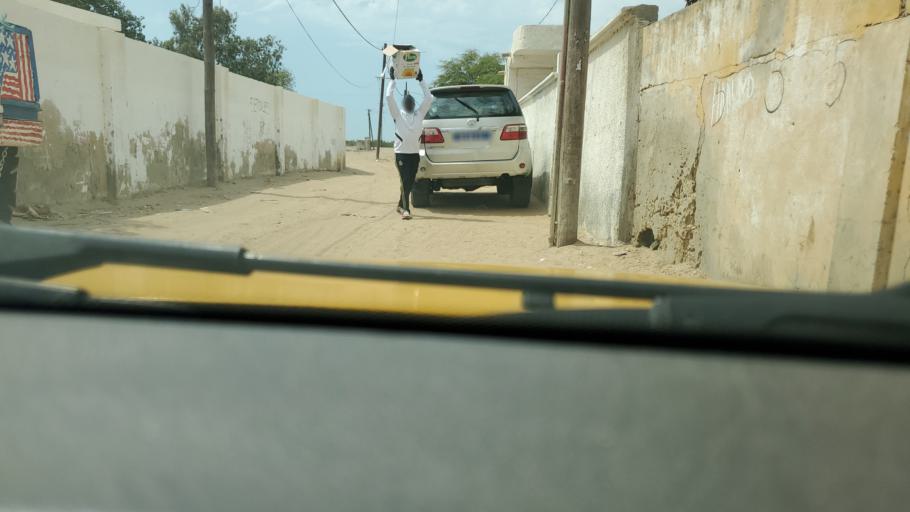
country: SN
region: Saint-Louis
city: Saint-Louis
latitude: 16.0263
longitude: -16.4754
